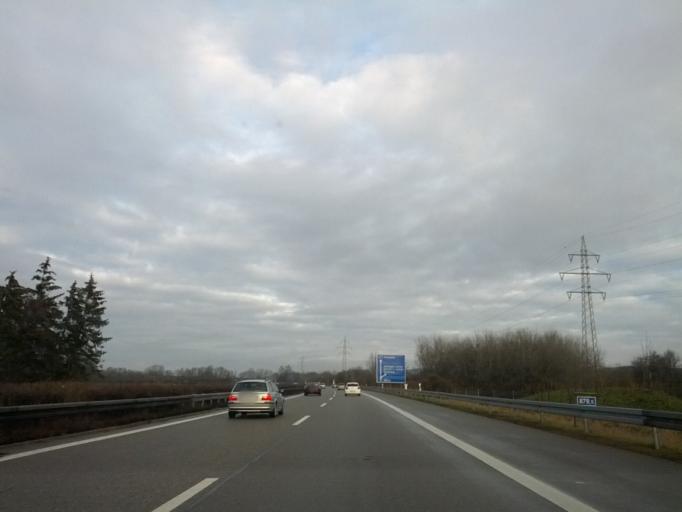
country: DE
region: Baden-Wuerttemberg
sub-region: Tuebingen Region
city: Dettingen an der Iller
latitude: 48.0988
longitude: 10.1329
